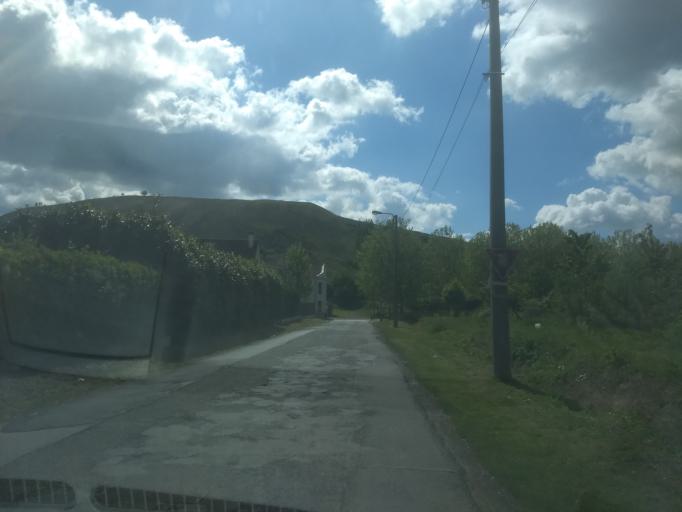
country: FR
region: Nord-Pas-de-Calais
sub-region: Departement du Pas-de-Calais
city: Drocourt
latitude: 50.4078
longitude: 2.9294
